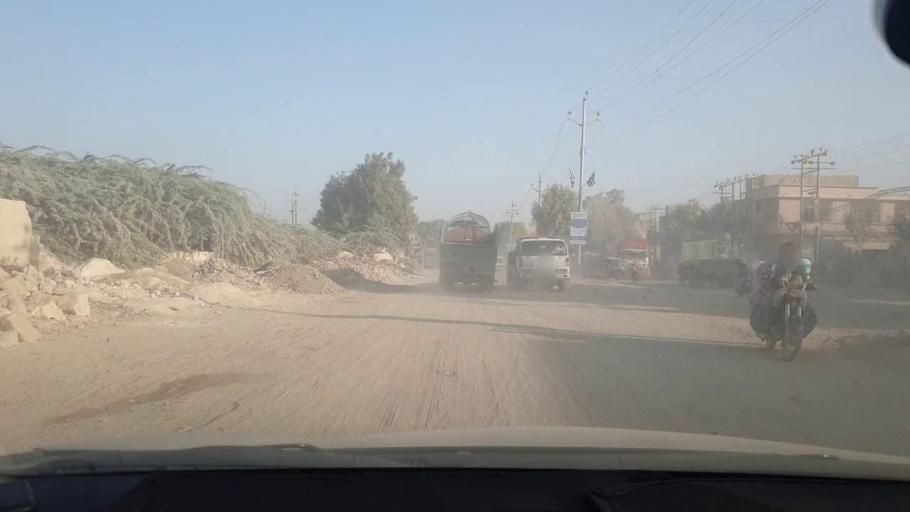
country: PK
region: Sindh
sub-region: Karachi District
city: Karachi
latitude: 24.9732
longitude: 67.0398
